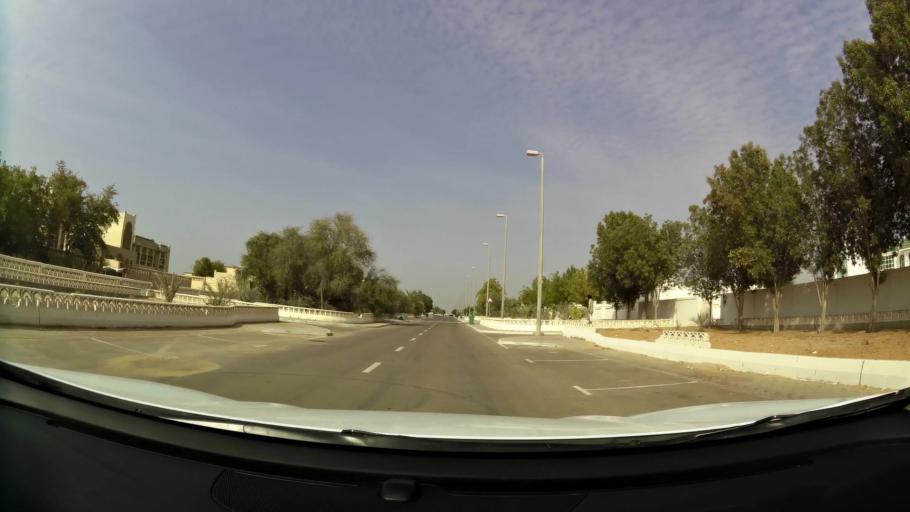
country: AE
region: Abu Dhabi
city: Abu Dhabi
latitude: 24.6096
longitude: 54.7032
